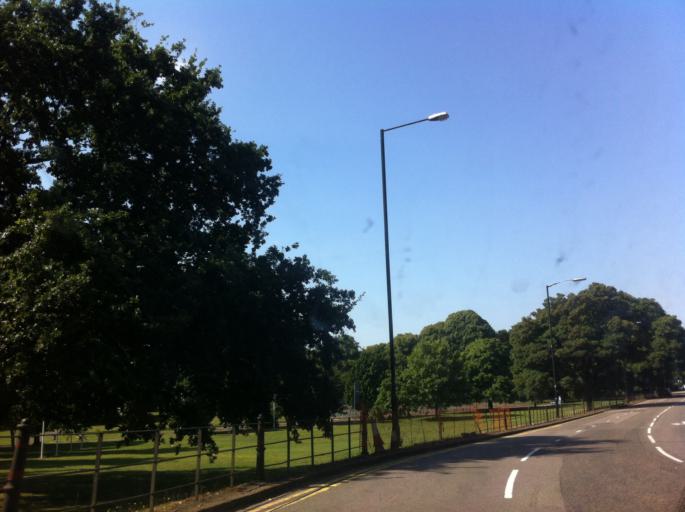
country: GB
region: England
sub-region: Northamptonshire
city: Northampton
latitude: 52.2347
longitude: -0.8875
